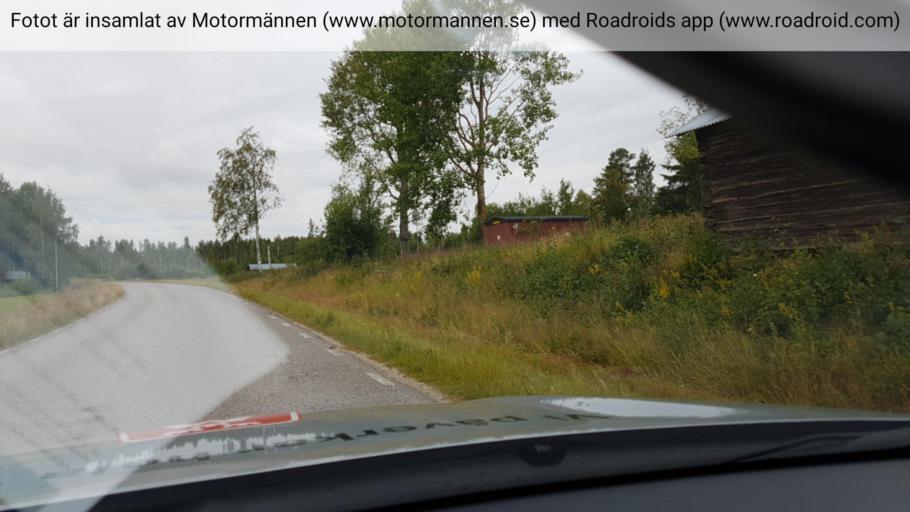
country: SE
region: Norrbotten
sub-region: Bodens Kommun
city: Saevast
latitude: 65.6746
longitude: 21.7951
